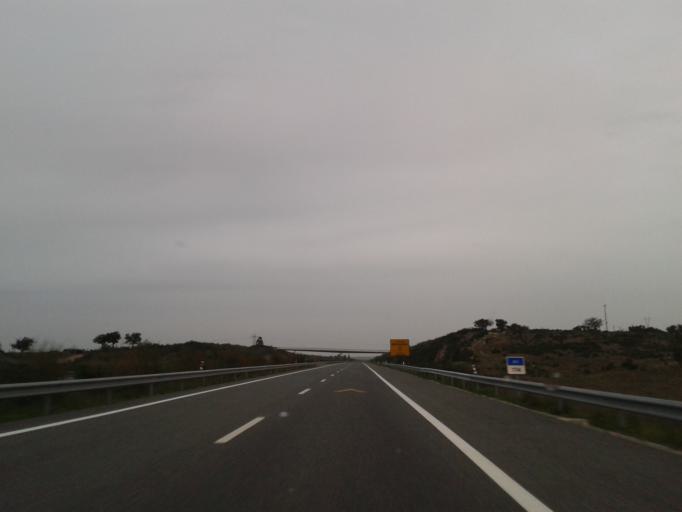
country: PT
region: Beja
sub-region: Ourique
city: Ourique
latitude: 37.6994
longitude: -8.1768
